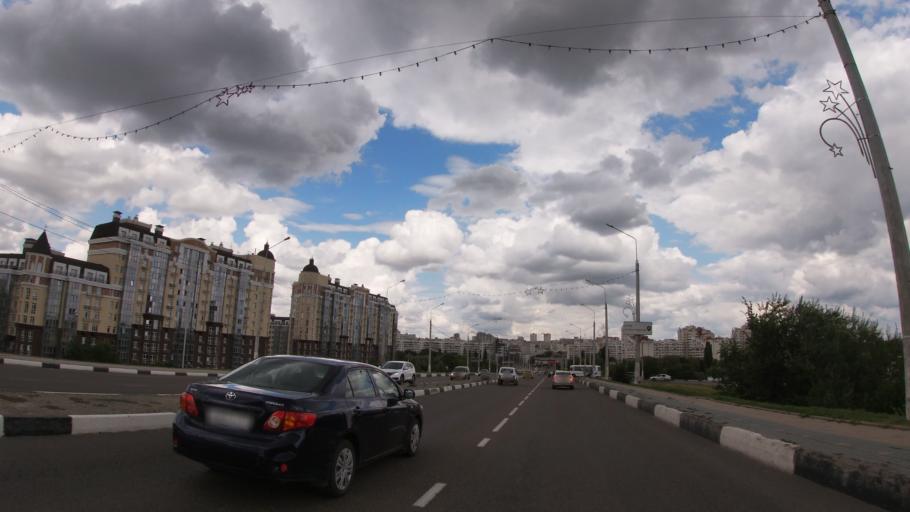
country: RU
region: Belgorod
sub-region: Belgorodskiy Rayon
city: Belgorod
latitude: 50.5874
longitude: 36.5881
